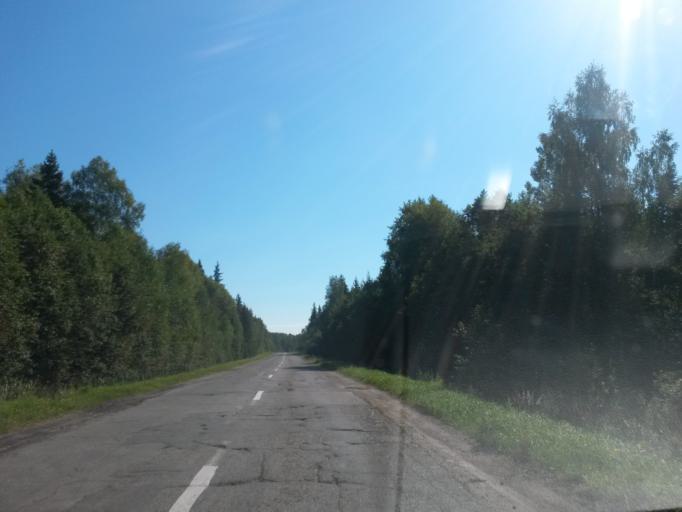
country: RU
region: Jaroslavl
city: Dubki
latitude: 57.2962
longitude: 40.0825
